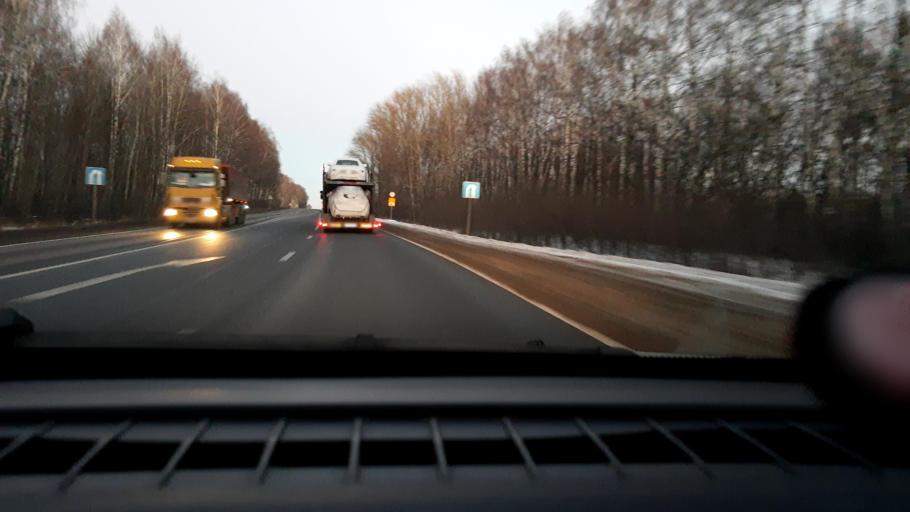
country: RU
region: Nizjnij Novgorod
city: Pervoye Maya
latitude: 55.9898
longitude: 44.7663
